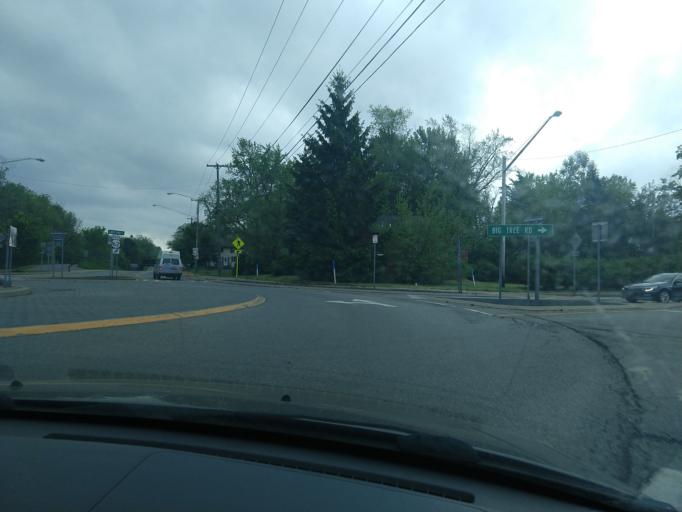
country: US
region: New York
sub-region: Erie County
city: Blasdell
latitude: 42.7720
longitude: -78.8240
